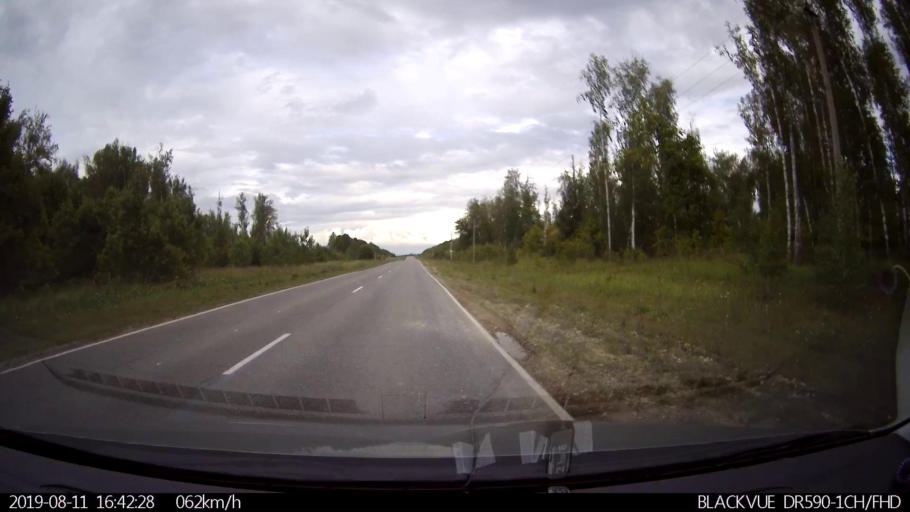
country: RU
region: Ulyanovsk
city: Mayna
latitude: 54.1607
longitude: 47.6625
